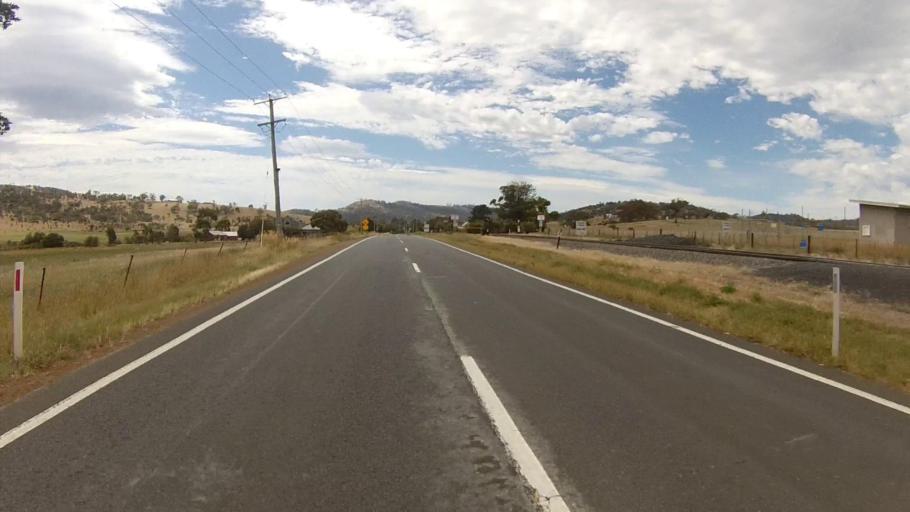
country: AU
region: Tasmania
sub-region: Brighton
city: Bridgewater
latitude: -42.6901
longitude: 147.3144
